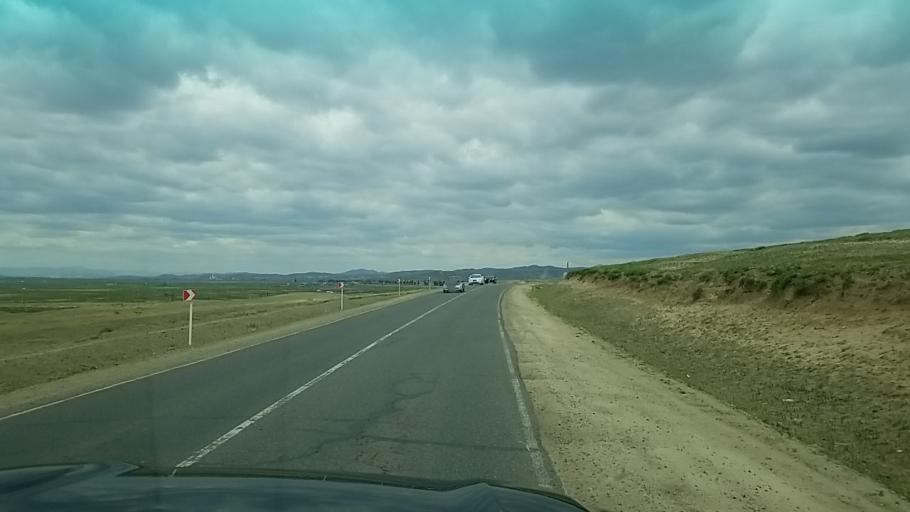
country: MN
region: Darhan Uul
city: Darhan
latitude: 49.4029
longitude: 105.9345
